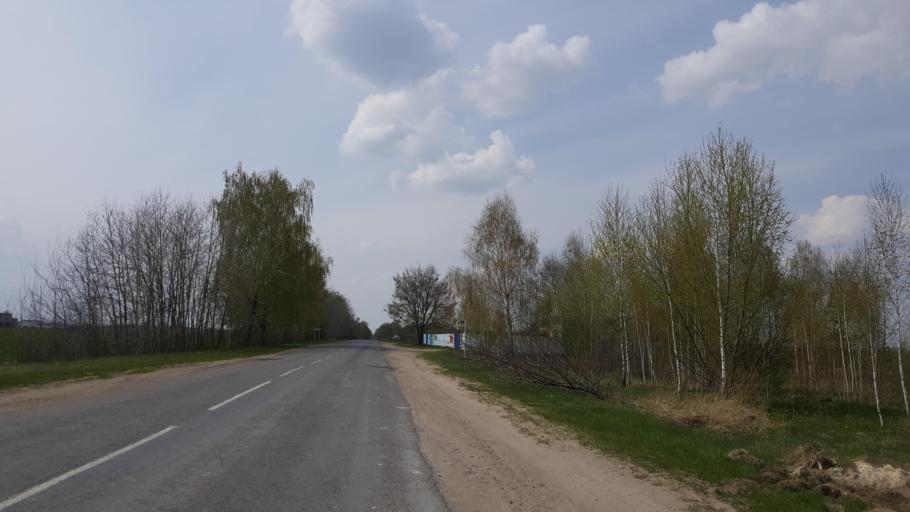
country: BY
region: Brest
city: Zhabinka
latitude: 52.2050
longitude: 23.9942
